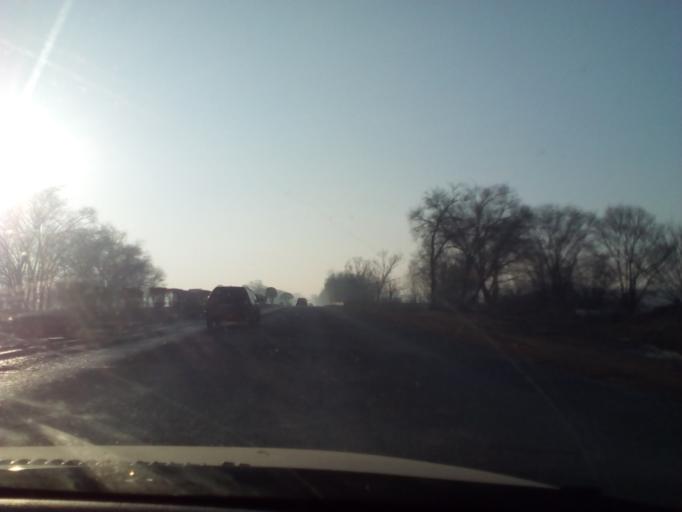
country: KZ
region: Almaty Oblysy
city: Burunday
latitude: 43.2235
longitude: 76.5963
